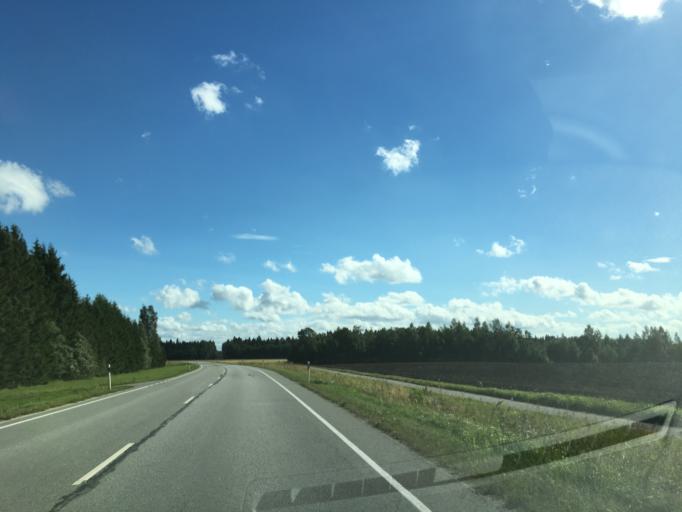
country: EE
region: Paernumaa
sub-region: Vaendra vald (alev)
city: Vandra
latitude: 58.6343
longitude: 25.0994
